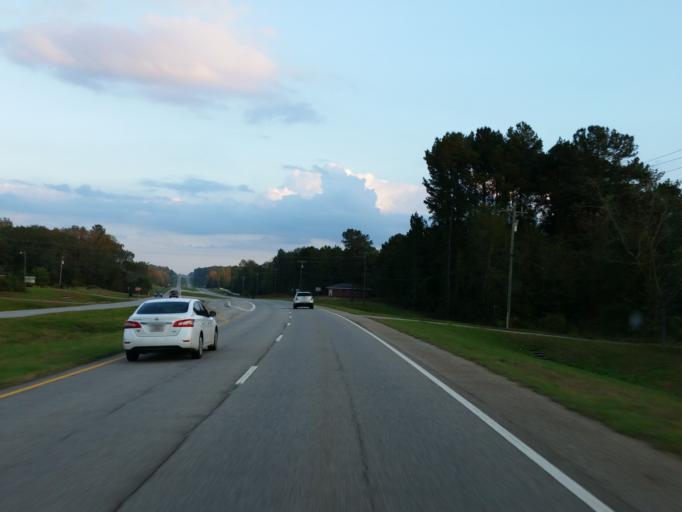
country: US
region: Georgia
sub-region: Houston County
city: Perry
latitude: 32.3701
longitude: -83.6154
